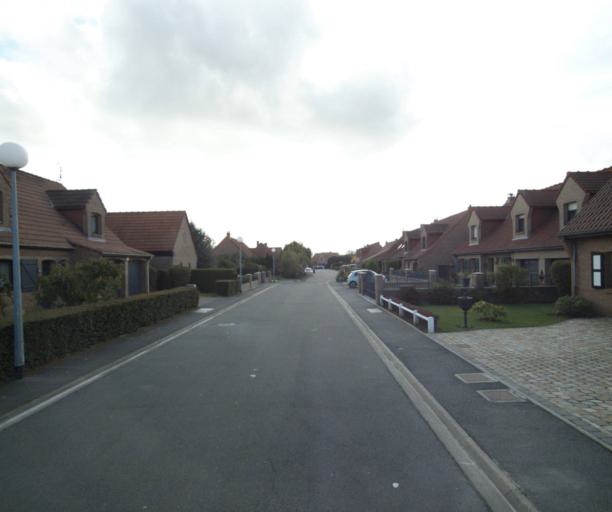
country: FR
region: Nord-Pas-de-Calais
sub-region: Departement du Nord
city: Houplines
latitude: 50.6924
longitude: 2.9197
